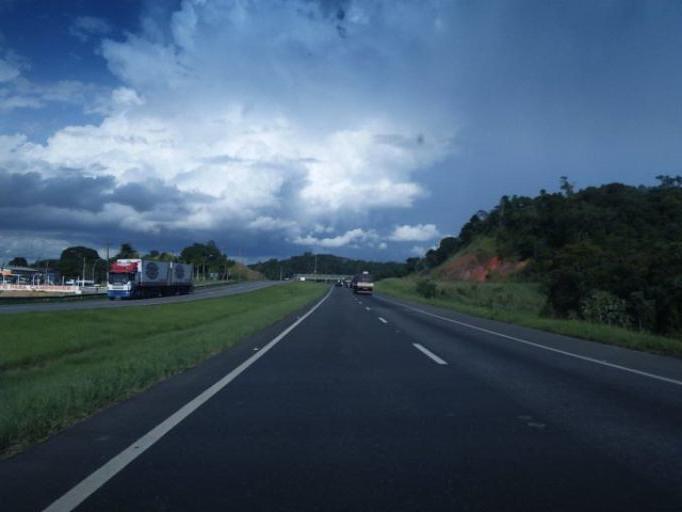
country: BR
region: Sao Paulo
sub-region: Juquia
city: Juquia
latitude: -24.3305
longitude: -47.6259
